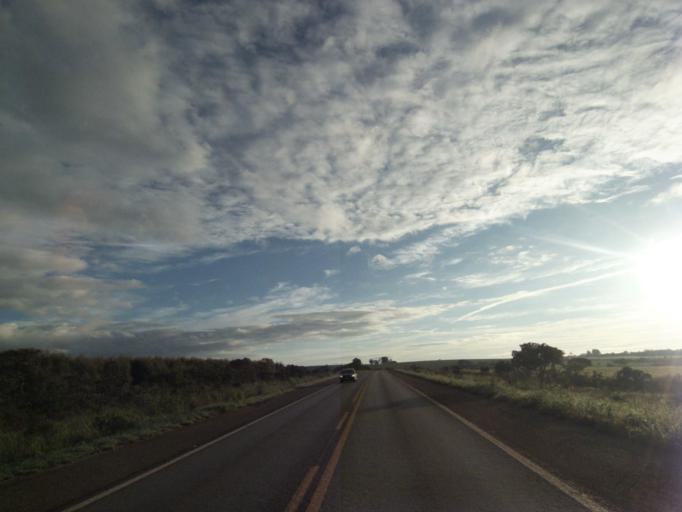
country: BR
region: Goias
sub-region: Pirenopolis
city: Pirenopolis
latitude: -15.7500
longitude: -48.6718
